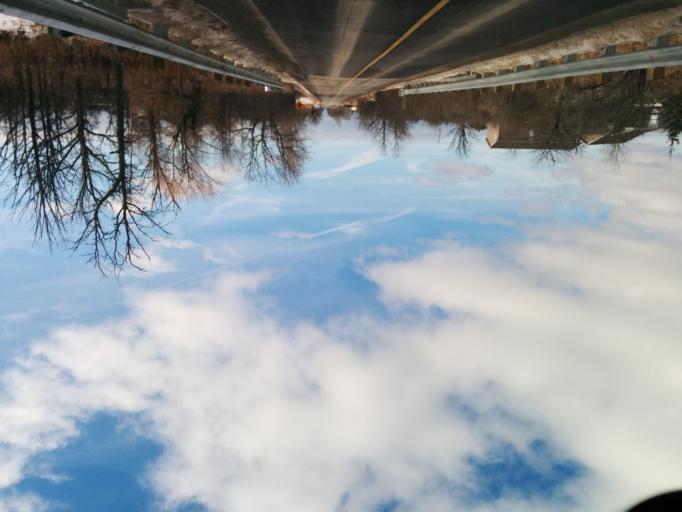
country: CA
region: Ontario
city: Brantford
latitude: 42.9903
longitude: -80.0728
